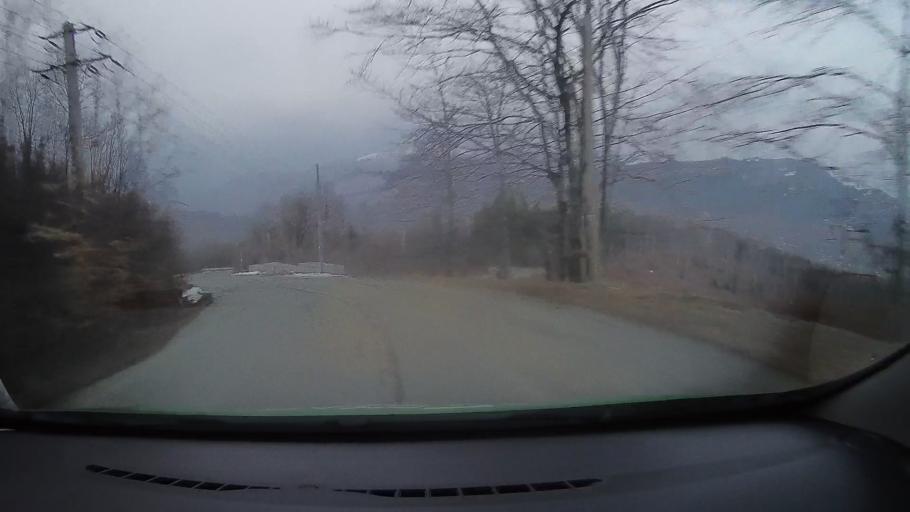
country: RO
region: Prahova
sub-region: Comuna Valea Doftanei
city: Tesila
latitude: 45.2918
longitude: 25.7056
